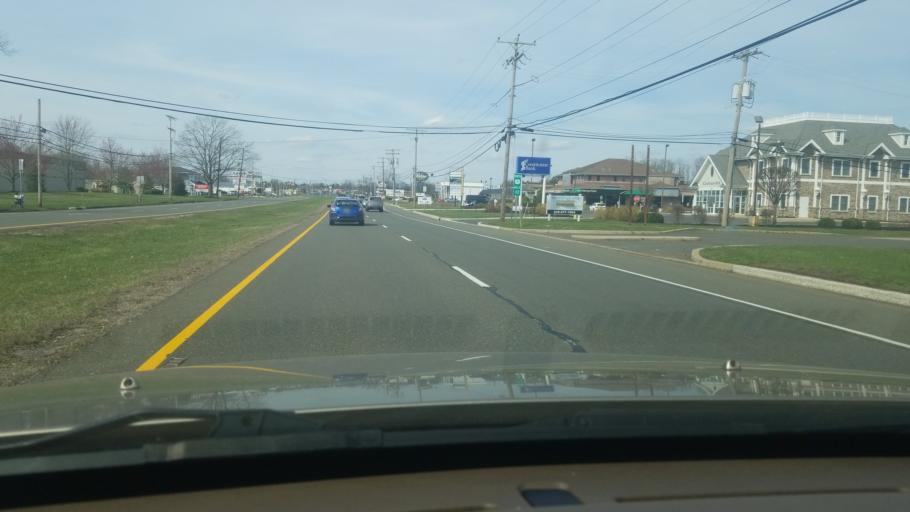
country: US
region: New Jersey
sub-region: Monmouth County
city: Freehold
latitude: 40.2296
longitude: -74.2723
